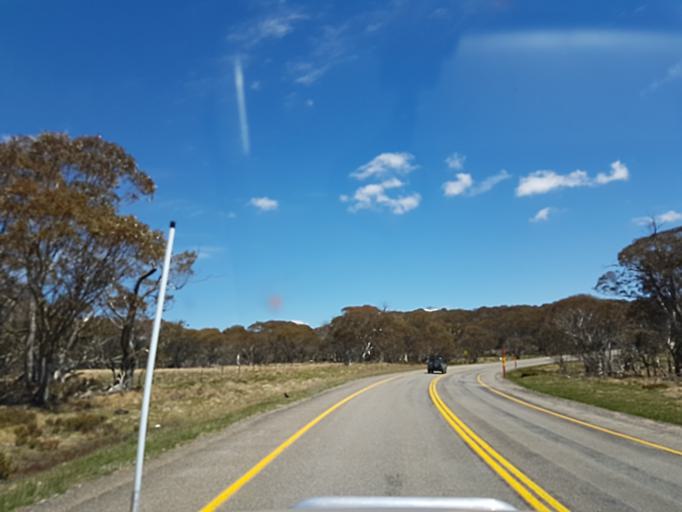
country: AU
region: Victoria
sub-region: Alpine
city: Mount Beauty
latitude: -37.0235
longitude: 147.2503
